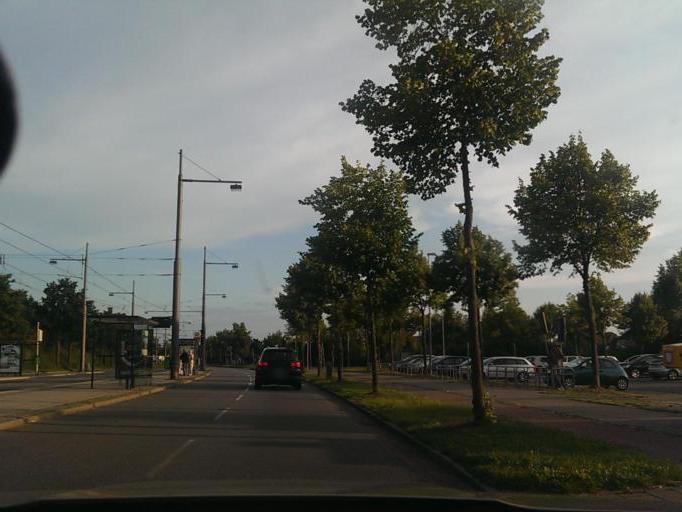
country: DE
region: Lower Saxony
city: Lilienthal
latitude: 53.1274
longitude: 8.8987
